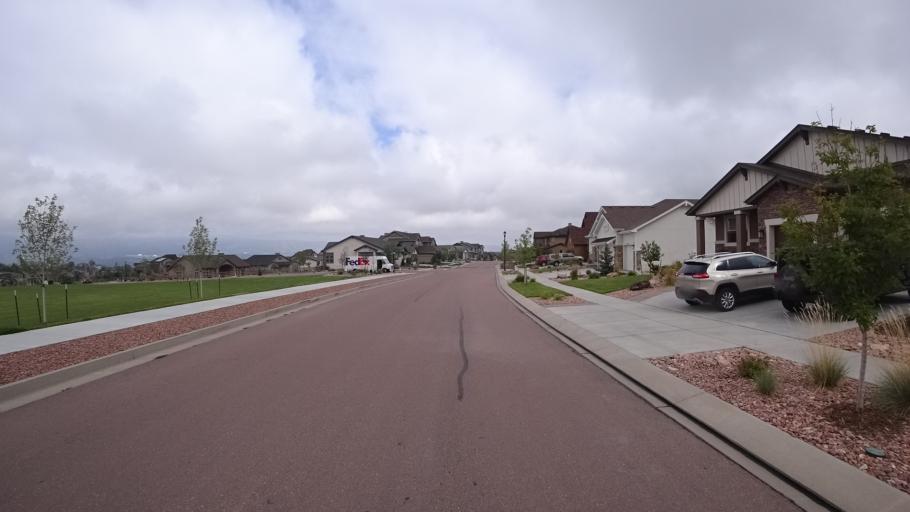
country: US
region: Colorado
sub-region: El Paso County
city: Gleneagle
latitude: 39.0114
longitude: -104.7891
